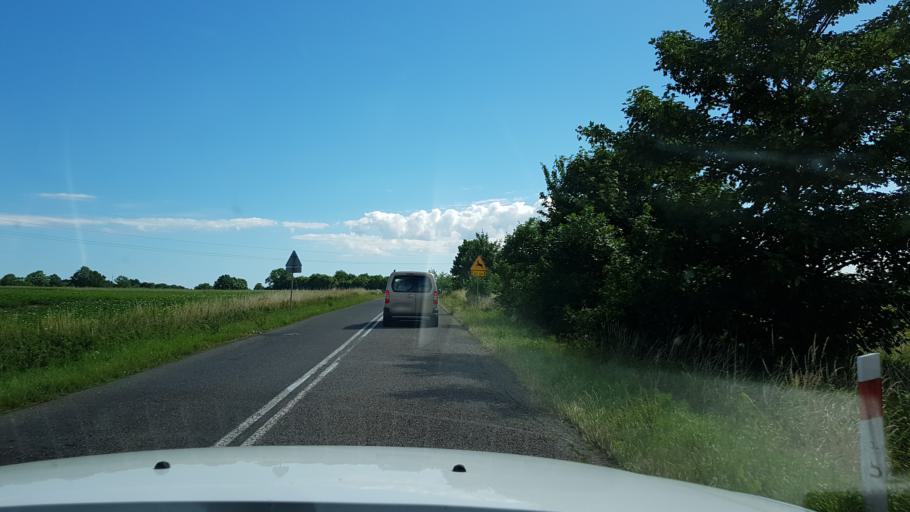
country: PL
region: West Pomeranian Voivodeship
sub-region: Powiat gryficki
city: Trzebiatow
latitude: 54.0411
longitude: 15.2224
